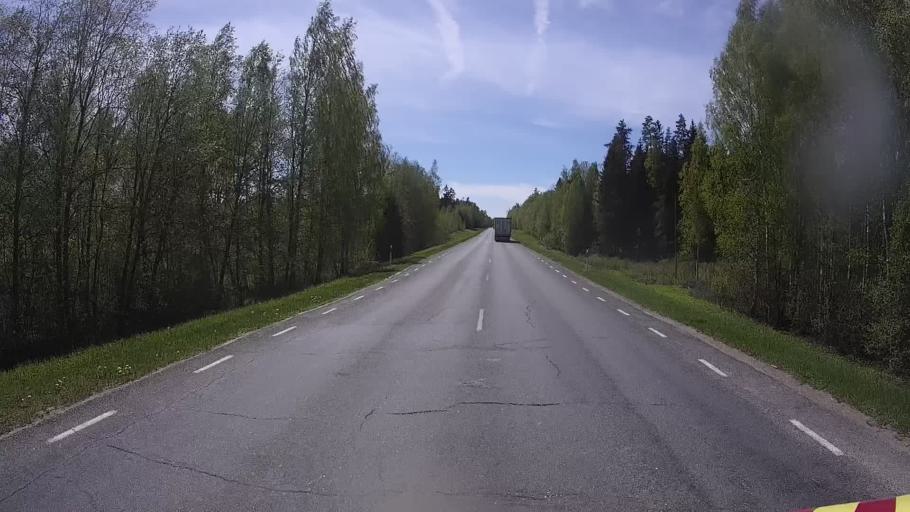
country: LV
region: Apes Novads
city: Ape
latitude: 57.7198
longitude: 26.7699
